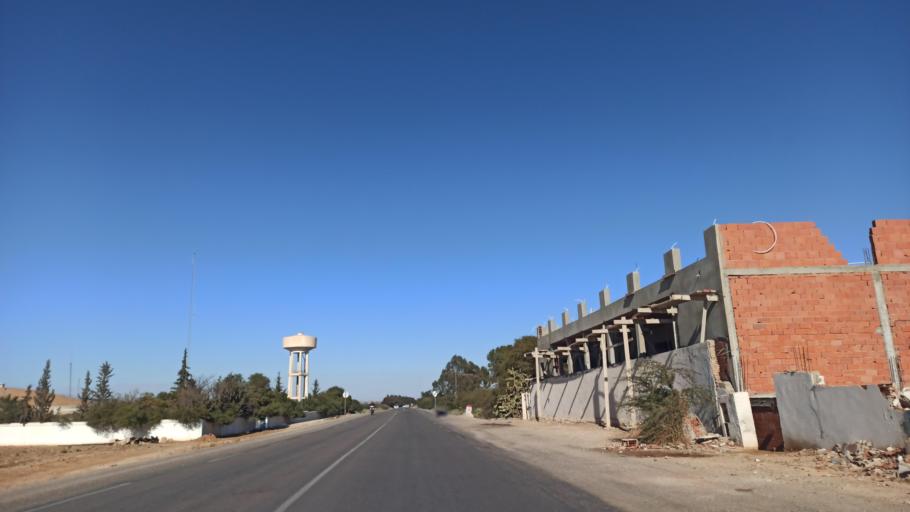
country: TN
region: Sidi Bu Zayd
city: Jilma
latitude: 35.1485
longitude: 9.3636
